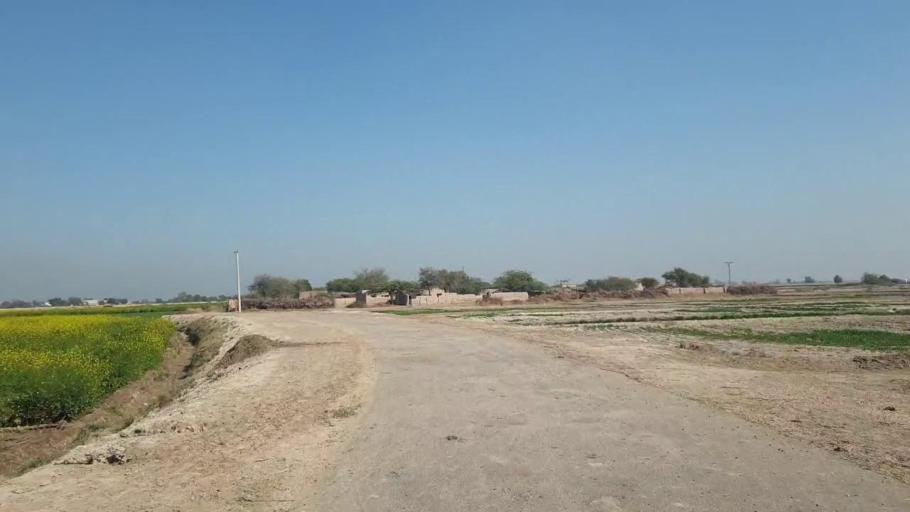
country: PK
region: Sindh
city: Shahpur Chakar
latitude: 26.1229
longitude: 68.6078
